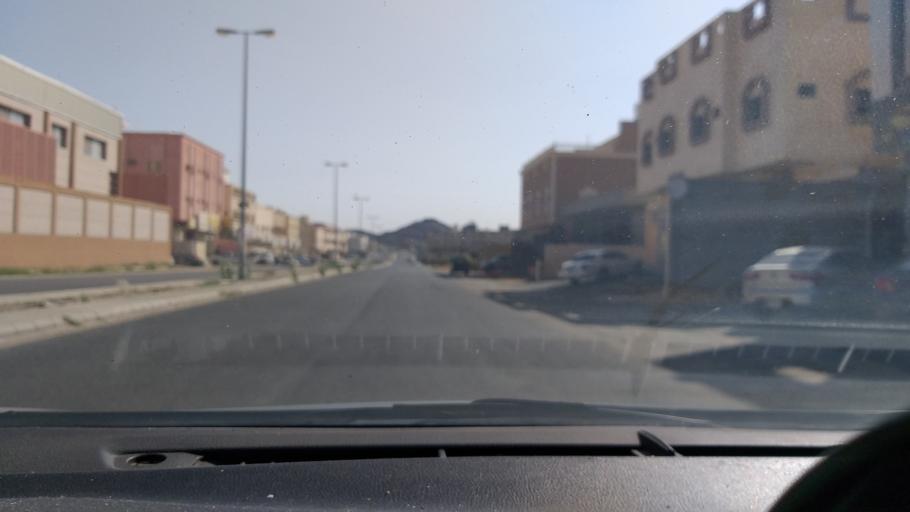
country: SA
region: Makkah
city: Ta'if
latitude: 21.2235
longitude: 40.3741
